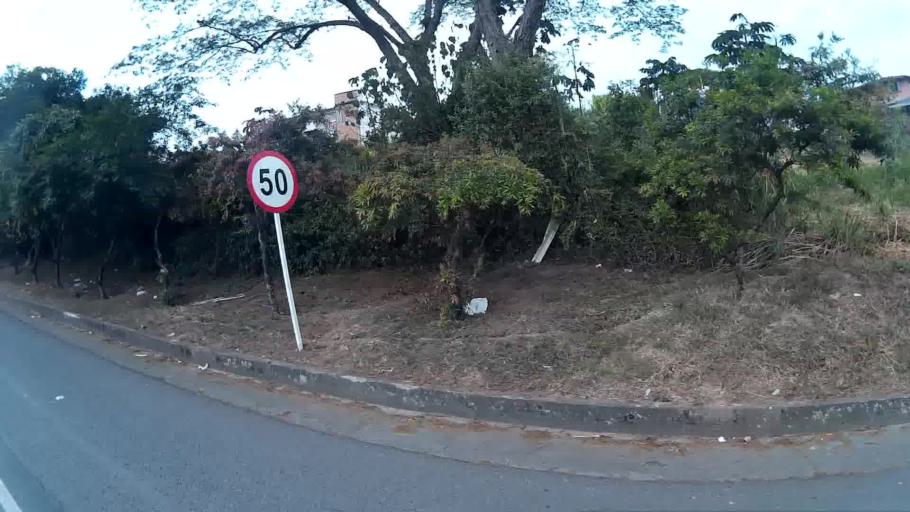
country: CO
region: Risaralda
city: Pereira
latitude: 4.8148
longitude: -75.7626
